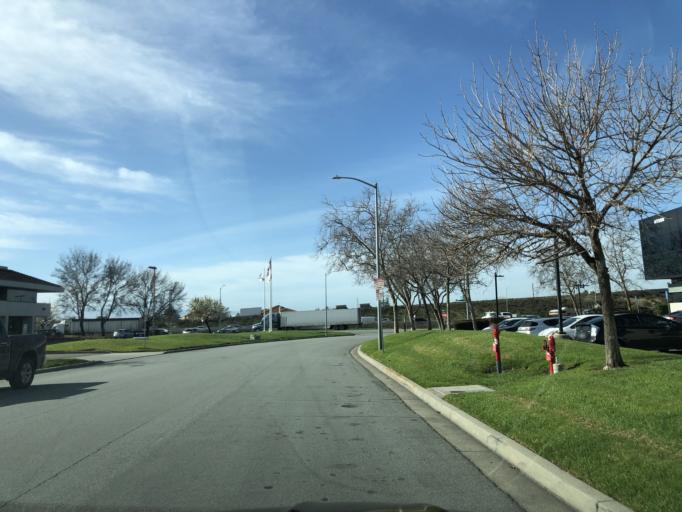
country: US
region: California
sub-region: Santa Clara County
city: Milpitas
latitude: 37.4807
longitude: -121.9328
